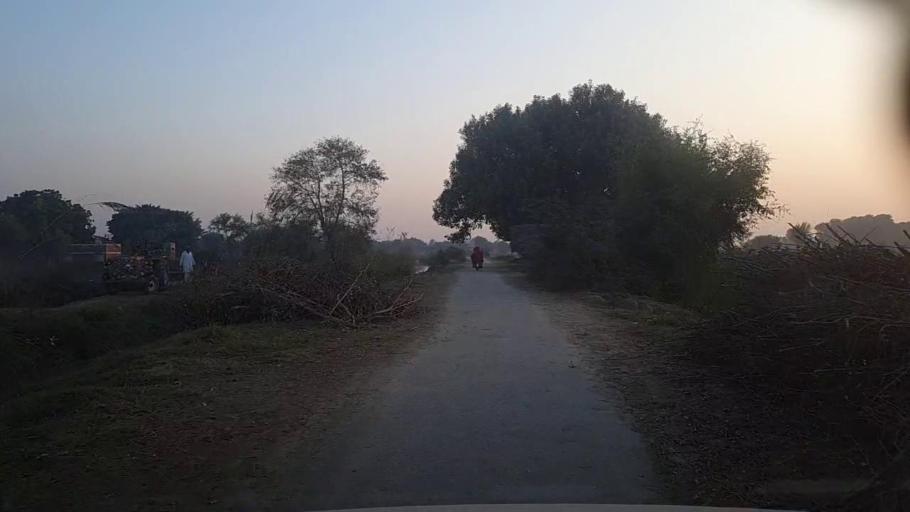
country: PK
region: Sindh
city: Karaundi
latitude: 26.8382
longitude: 68.3695
